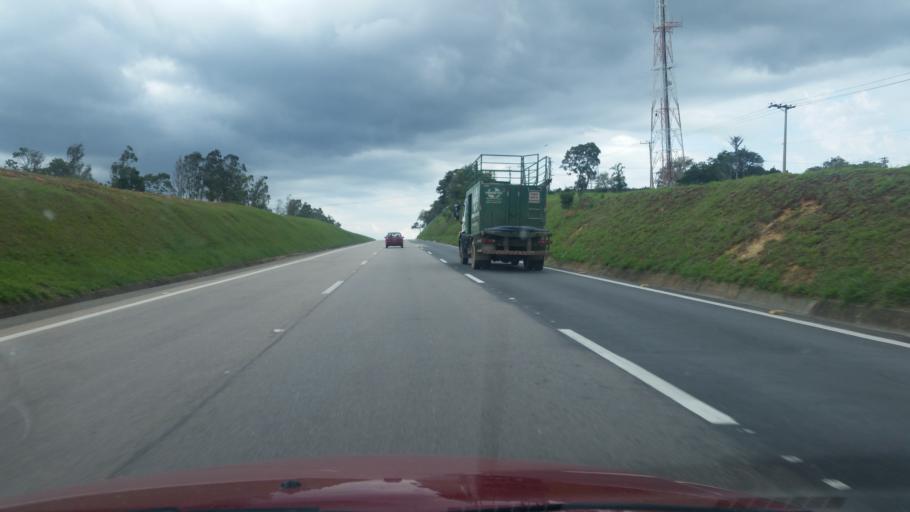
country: BR
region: Sao Paulo
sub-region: Sorocaba
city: Sorocaba
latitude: -23.3750
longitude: -47.4302
